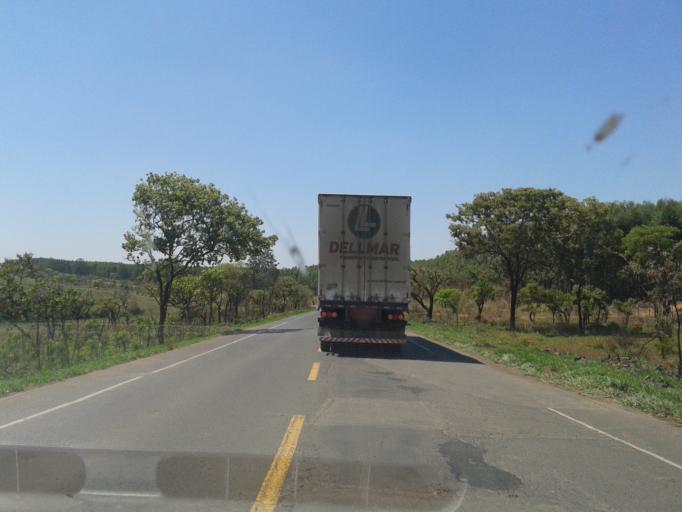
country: BR
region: Minas Gerais
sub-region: Araxa
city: Araxa
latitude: -19.4352
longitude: -47.2151
